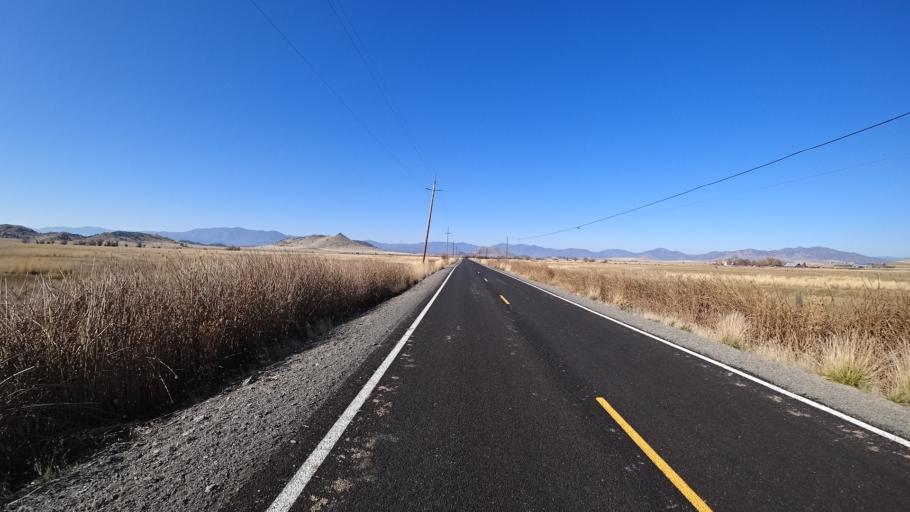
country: US
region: California
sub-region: Siskiyou County
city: Montague
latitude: 41.7114
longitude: -122.4293
